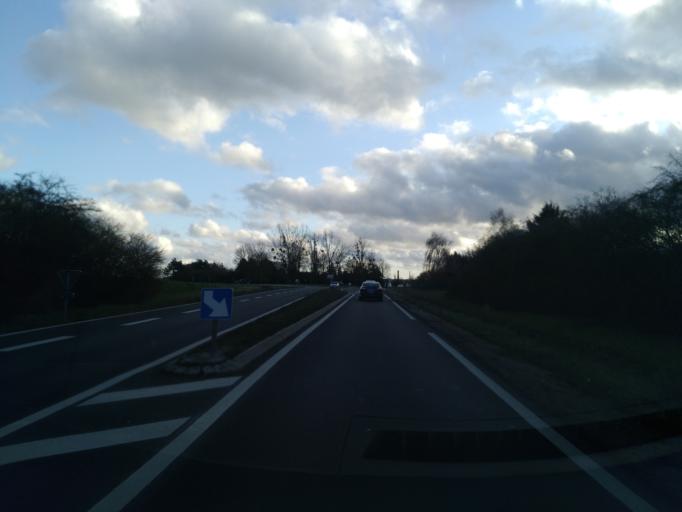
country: FR
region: Ile-de-France
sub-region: Departement des Yvelines
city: Feucherolles
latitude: 48.8662
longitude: 1.9685
